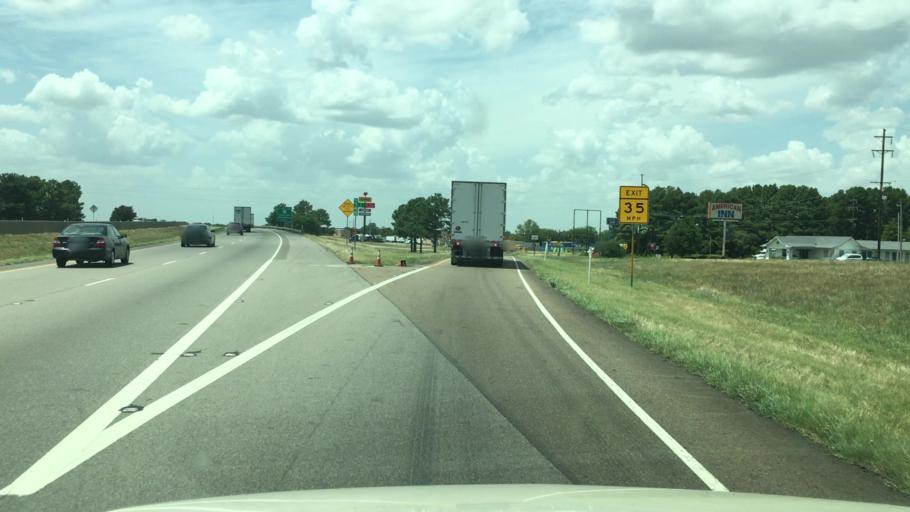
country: US
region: Texas
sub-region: Franklin County
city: Mount Vernon
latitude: 33.1624
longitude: -95.2134
